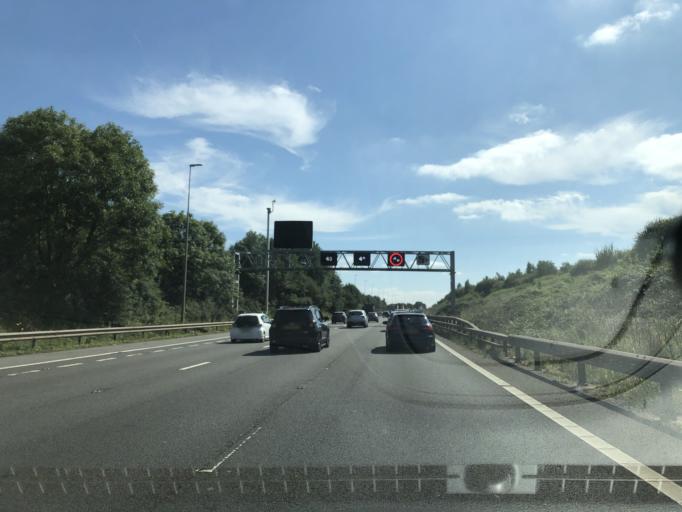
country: GB
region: England
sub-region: Solihull
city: Chelmsley Wood
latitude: 52.4889
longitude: -1.7121
